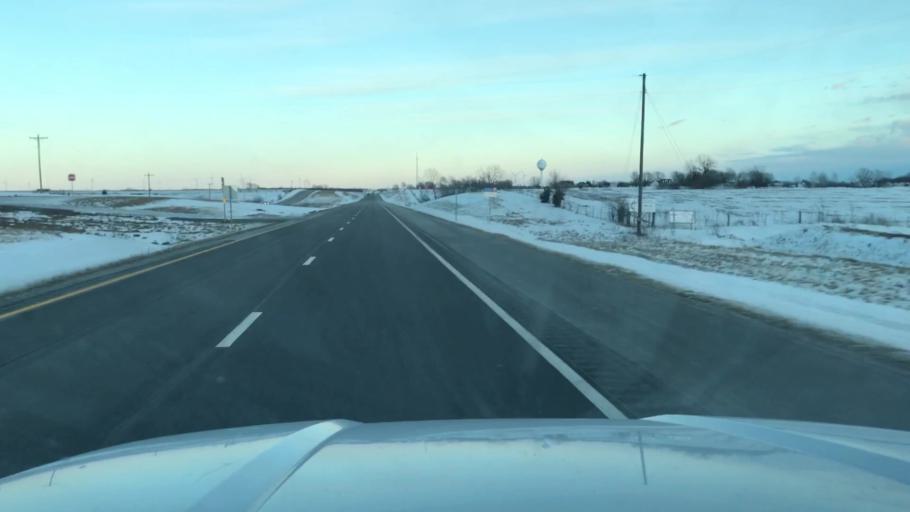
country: US
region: Missouri
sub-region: Clinton County
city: Gower
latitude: 39.7620
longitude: -94.5180
